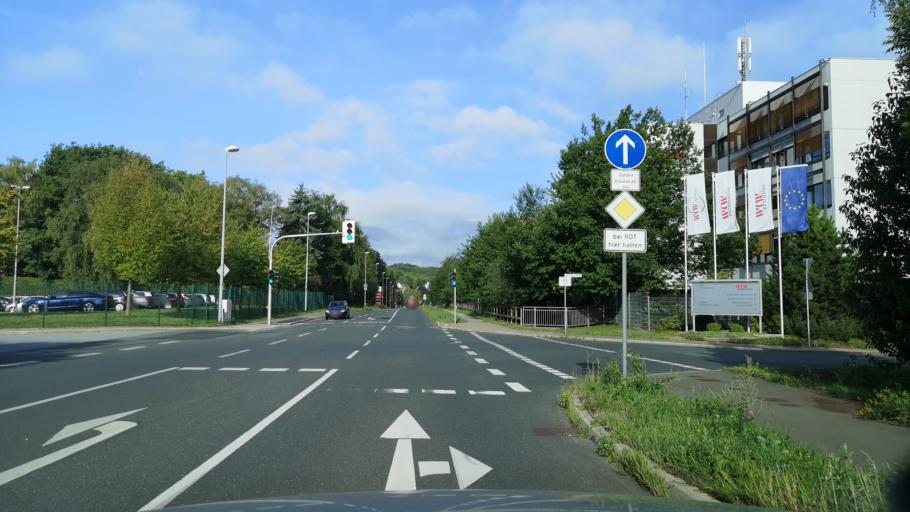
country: DE
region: North Rhine-Westphalia
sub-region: Regierungsbezirk Dusseldorf
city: Wuppertal
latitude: 51.3088
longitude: 7.1105
